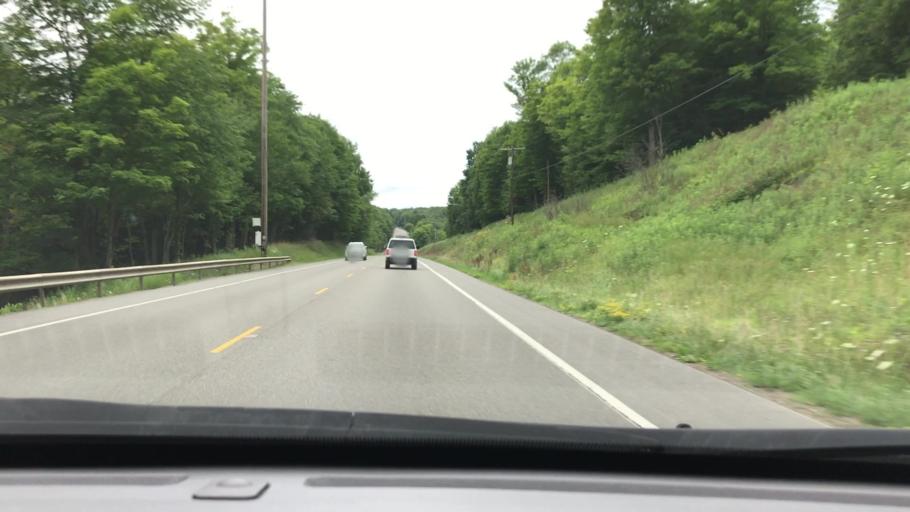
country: US
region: Pennsylvania
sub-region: McKean County
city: Kane
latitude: 41.6918
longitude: -78.6904
